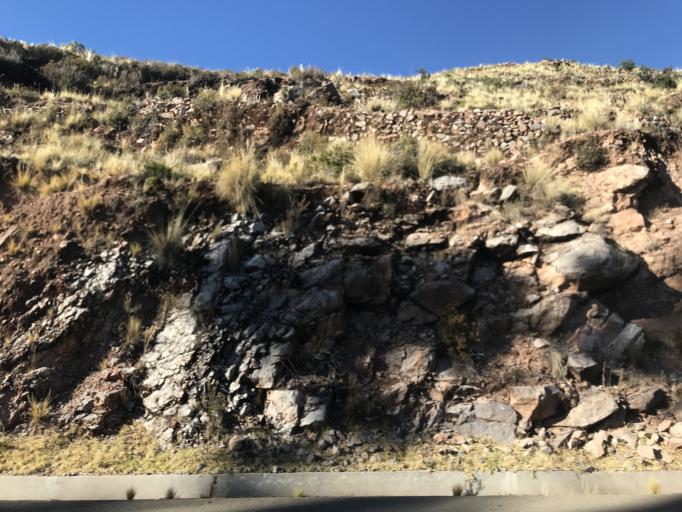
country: BO
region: La Paz
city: San Pedro
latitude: -16.1920
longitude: -68.9177
